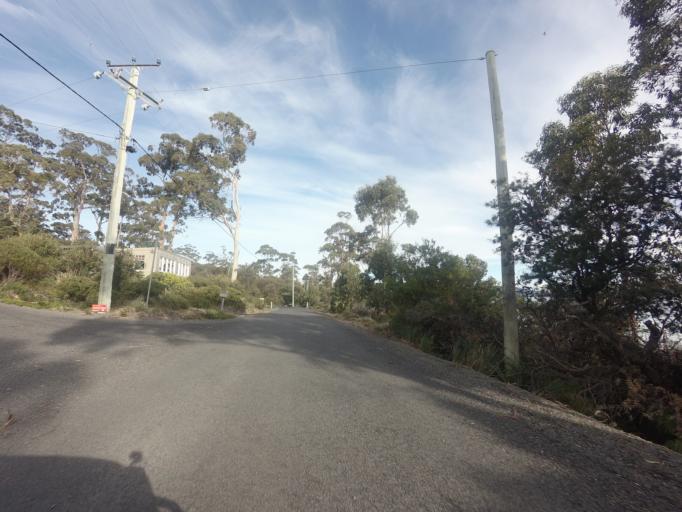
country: AU
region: Tasmania
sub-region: Sorell
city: Sorell
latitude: -42.9726
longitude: 147.8354
